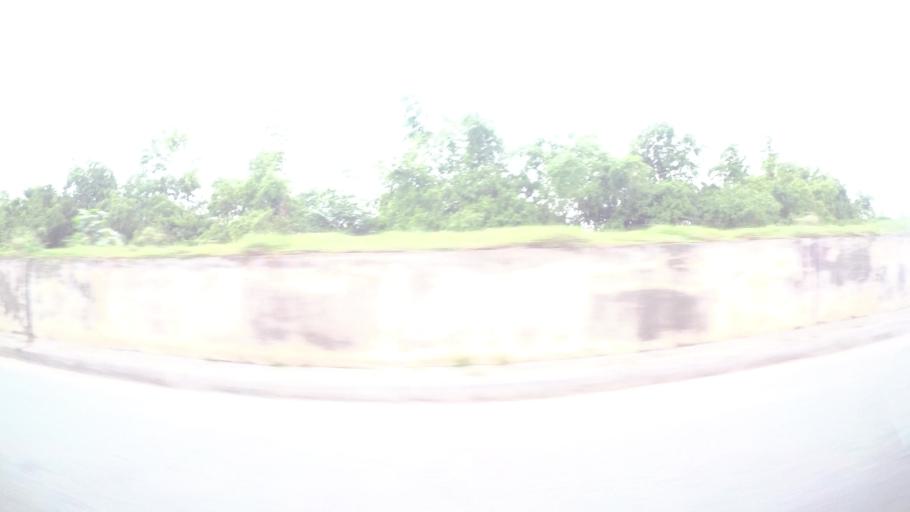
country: VN
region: Ha Noi
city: Trau Quy
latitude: 21.0554
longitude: 105.9200
